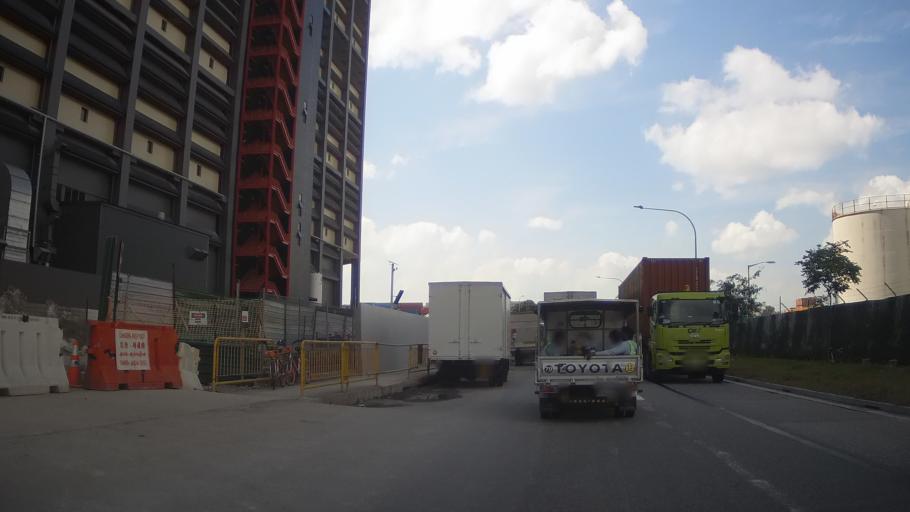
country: SG
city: Singapore
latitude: 1.3163
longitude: 103.7152
